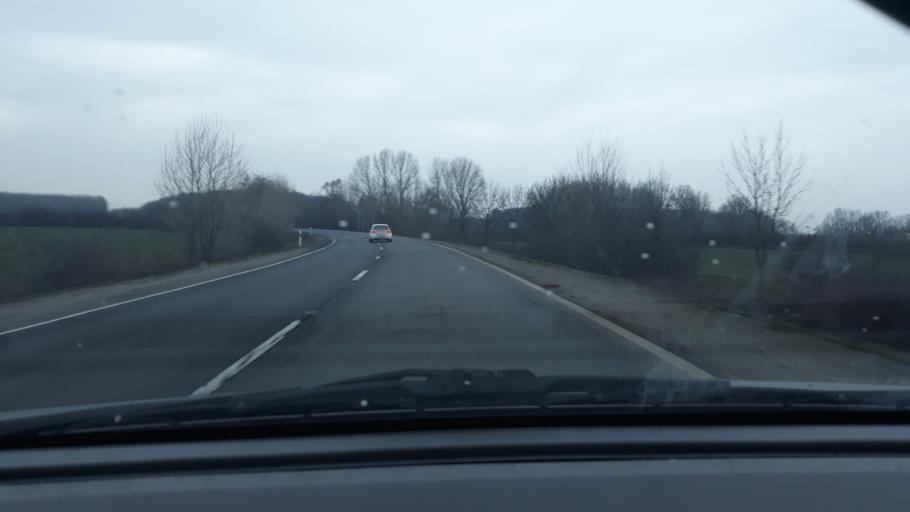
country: HU
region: Hajdu-Bihar
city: Biharkeresztes
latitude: 47.1376
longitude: 21.7383
